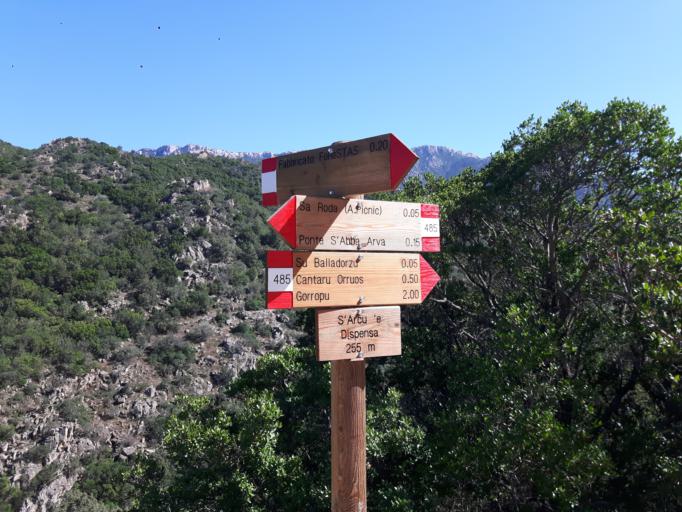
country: IT
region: Sardinia
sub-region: Provincia di Nuoro
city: Dorgali
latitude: 40.2171
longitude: 9.5178
